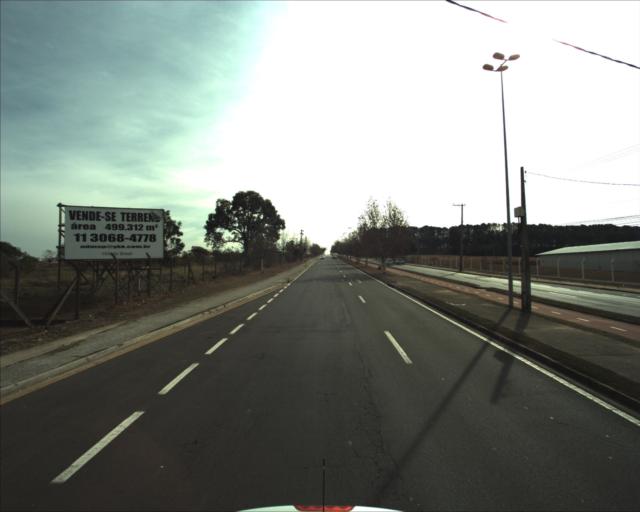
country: BR
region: Sao Paulo
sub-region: Sorocaba
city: Sorocaba
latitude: -23.4640
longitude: -47.4524
